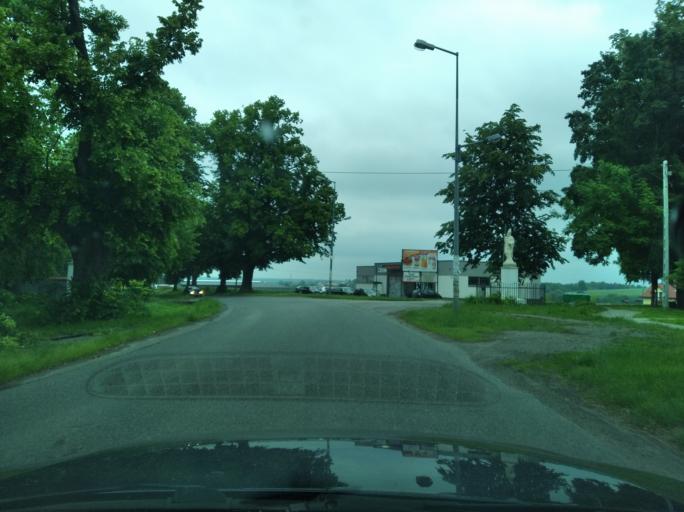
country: PL
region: Subcarpathian Voivodeship
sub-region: Powiat ropczycko-sedziszowski
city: Sedziszow Malopolski
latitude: 50.0570
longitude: 21.6893
